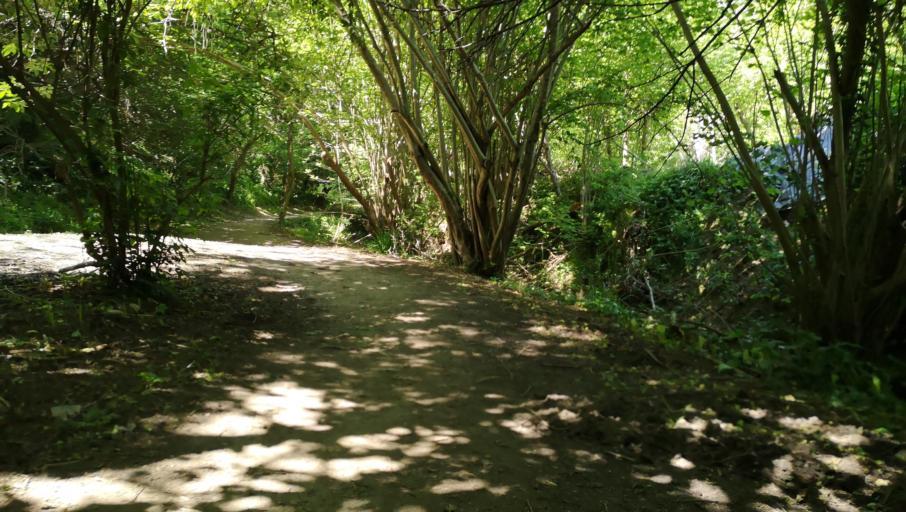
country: FR
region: Midi-Pyrenees
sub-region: Departement de la Haute-Garonne
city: Beauzelle
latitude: 43.6598
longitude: 1.3924
